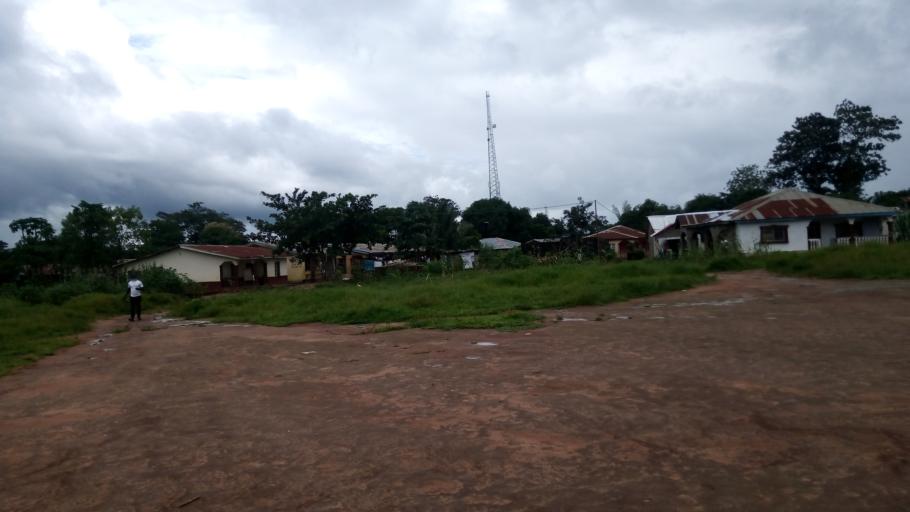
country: SL
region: Northern Province
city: Lunsar
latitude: 8.6923
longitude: -12.5301
